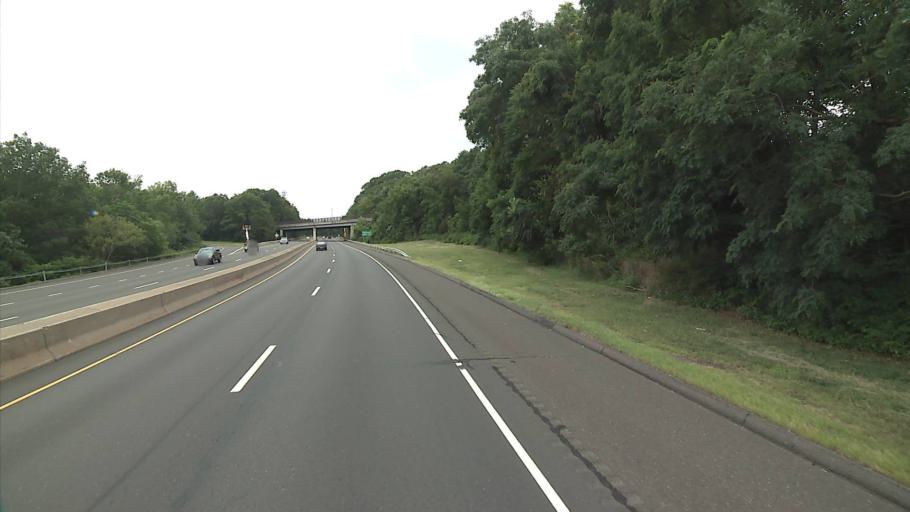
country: US
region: Connecticut
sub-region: New Haven County
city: Ansonia
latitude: 41.3611
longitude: -73.0929
